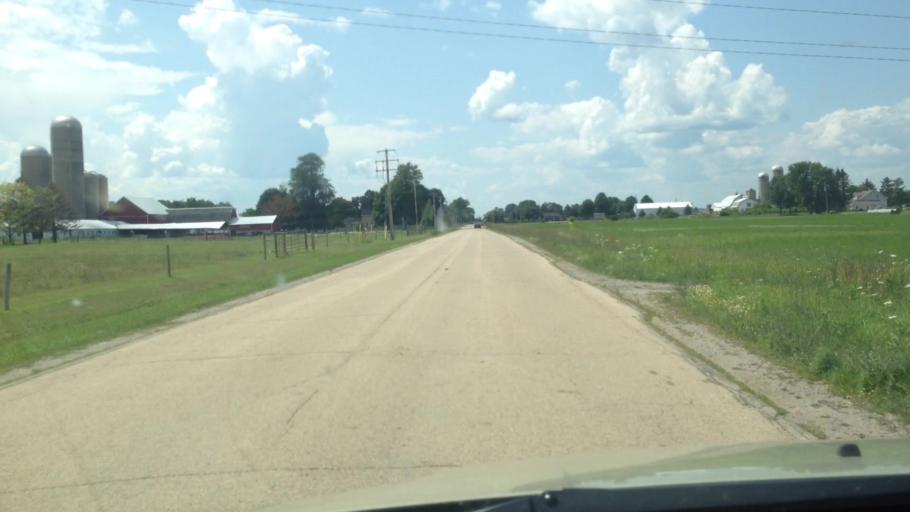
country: US
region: Wisconsin
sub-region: Brown County
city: Pulaski
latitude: 44.6567
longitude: -88.2525
